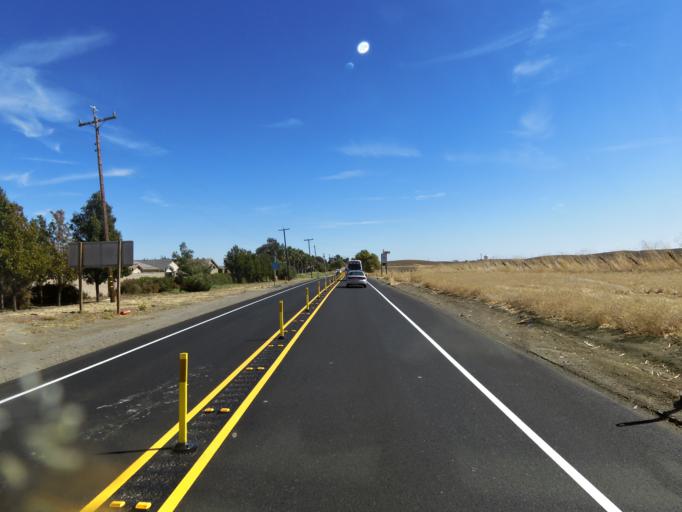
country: US
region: California
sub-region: Solano County
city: Rio Vista
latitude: 38.1792
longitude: -121.7202
